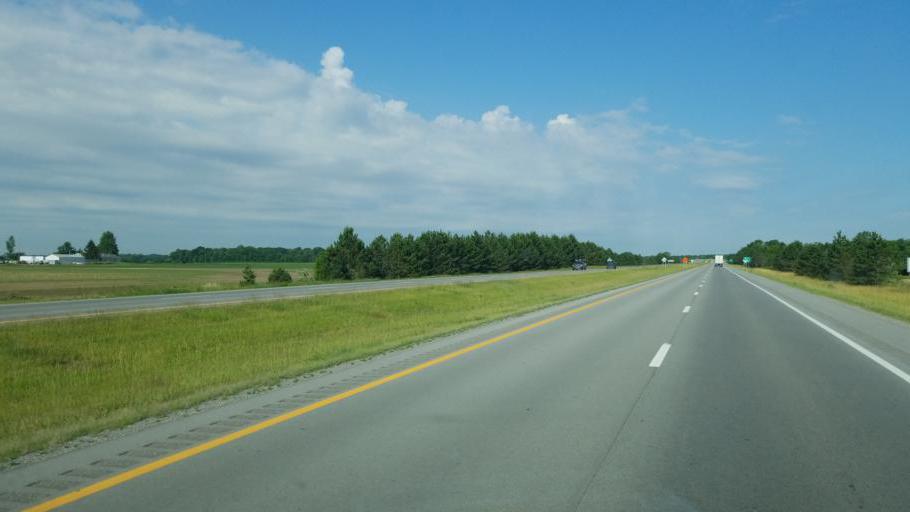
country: US
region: Ohio
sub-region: Hancock County
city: Findlay
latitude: 40.9864
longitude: -83.6251
